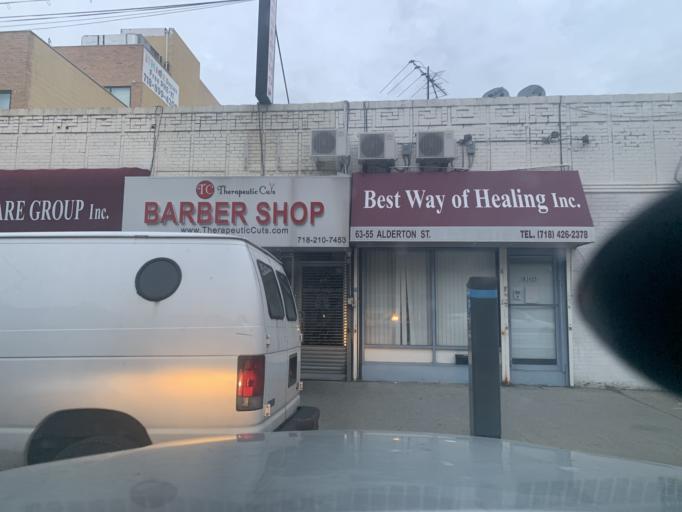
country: US
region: New York
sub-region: Queens County
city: Borough of Queens
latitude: 40.7263
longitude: -73.8652
